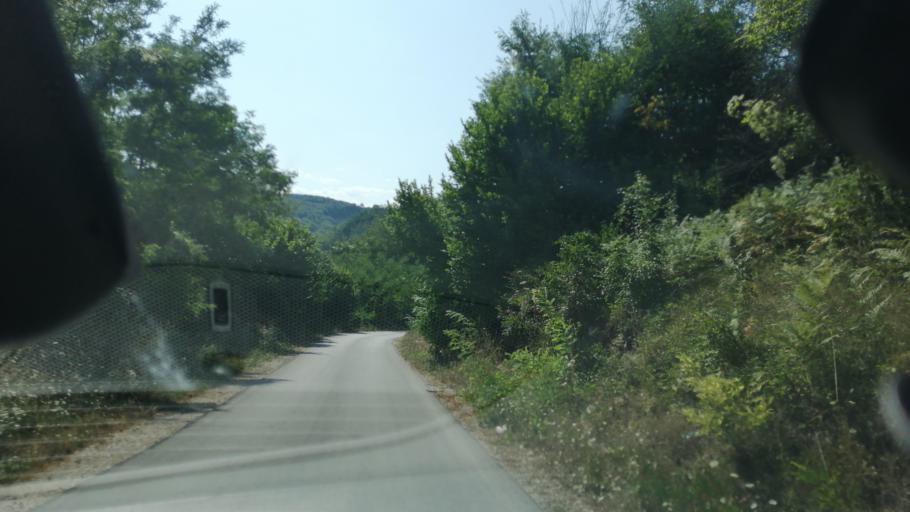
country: RS
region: Central Serbia
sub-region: Moravicki Okrug
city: Ivanjica
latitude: 43.6234
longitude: 20.2449
